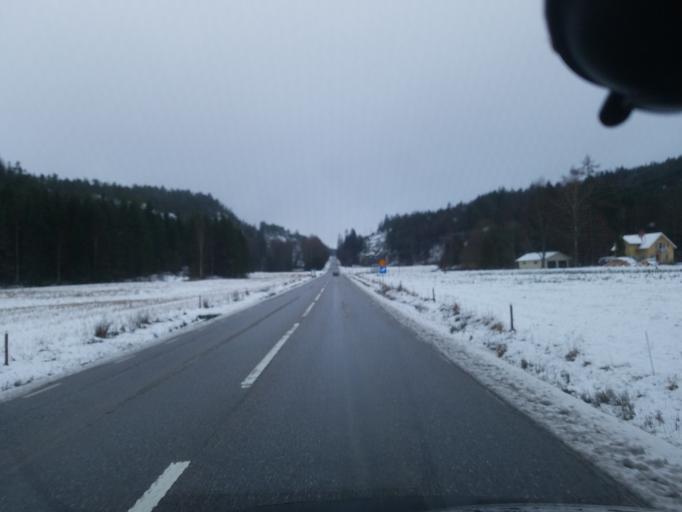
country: SE
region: Vaestra Goetaland
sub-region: Orust
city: Henan
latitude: 58.3228
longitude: 11.6323
